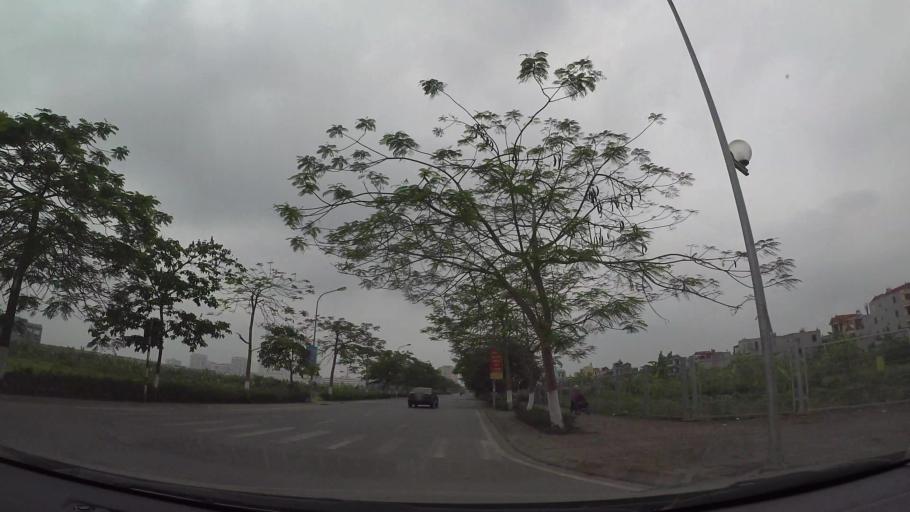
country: VN
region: Ha Noi
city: Trau Quy
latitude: 21.0511
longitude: 105.9214
